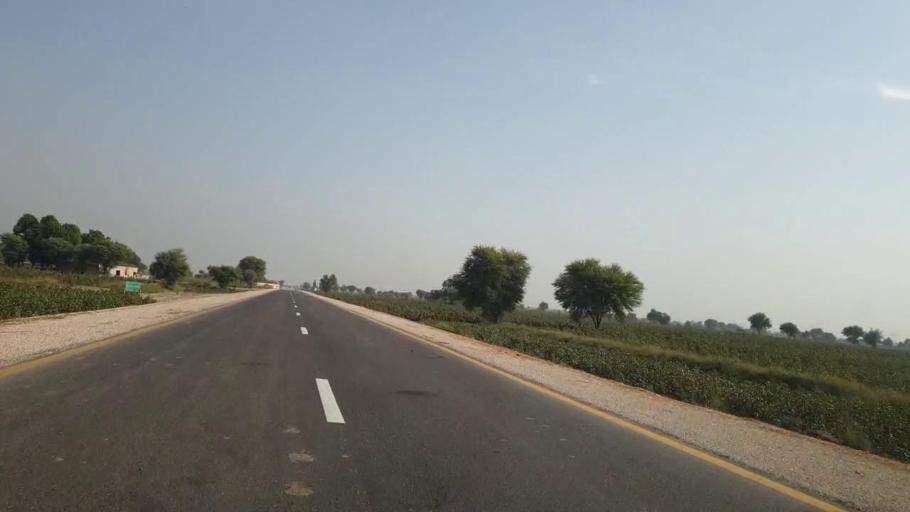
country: PK
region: Sindh
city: Sehwan
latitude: 26.4733
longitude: 67.7895
